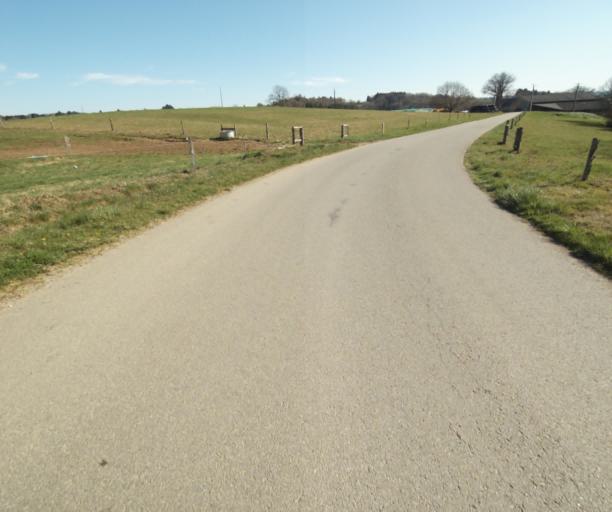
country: FR
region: Limousin
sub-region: Departement de la Correze
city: Chamboulive
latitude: 45.4755
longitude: 1.7190
